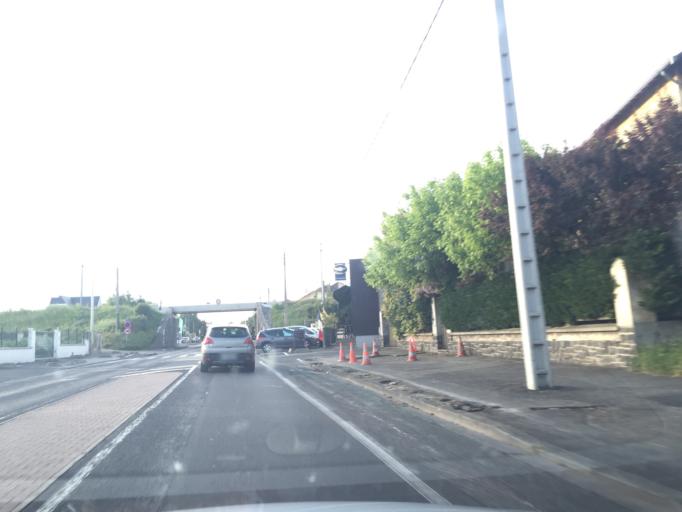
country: FR
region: Auvergne
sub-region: Departement du Puy-de-Dome
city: Menetrol
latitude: 45.8829
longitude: 3.1161
